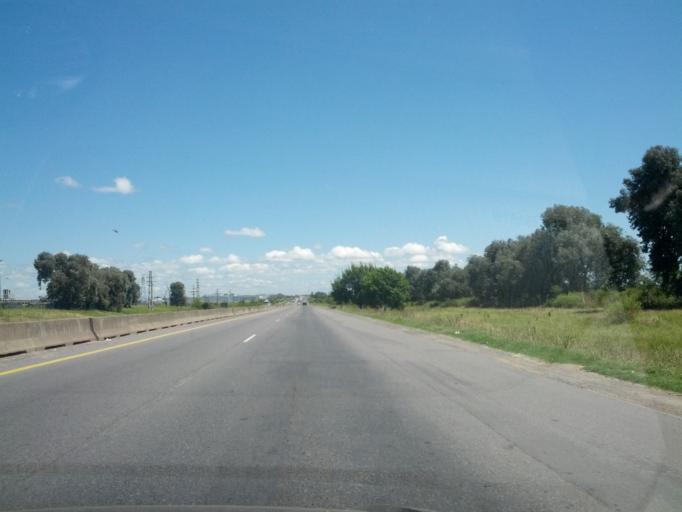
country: AR
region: Buenos Aires
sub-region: Partido de Zarate
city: Zarate
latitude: -34.1246
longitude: -59.0239
